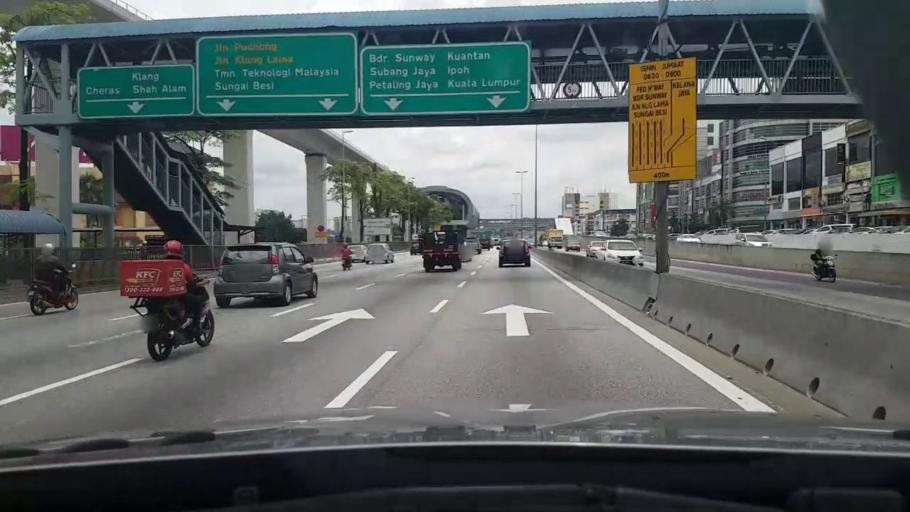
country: MY
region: Selangor
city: Subang Jaya
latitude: 3.0447
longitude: 101.6196
